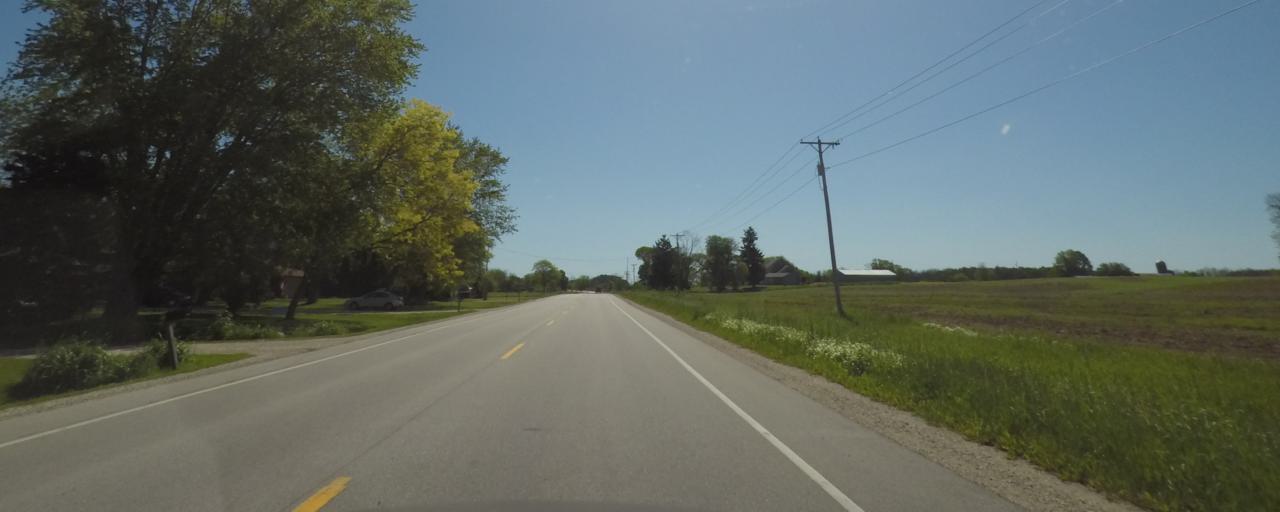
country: US
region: Wisconsin
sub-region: Sheboygan County
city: Plymouth
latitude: 43.7464
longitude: -87.9263
